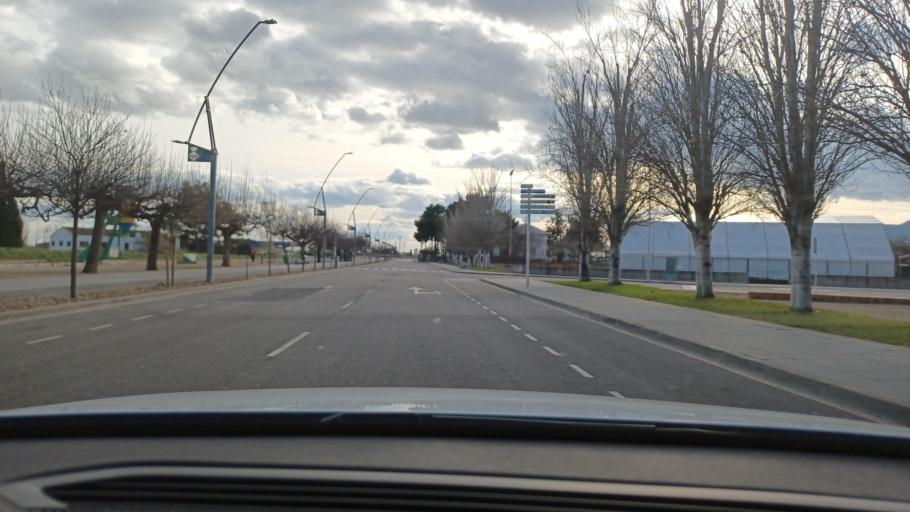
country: ES
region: Catalonia
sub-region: Provincia de Tarragona
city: Amposta
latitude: 40.7063
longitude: 0.5856
